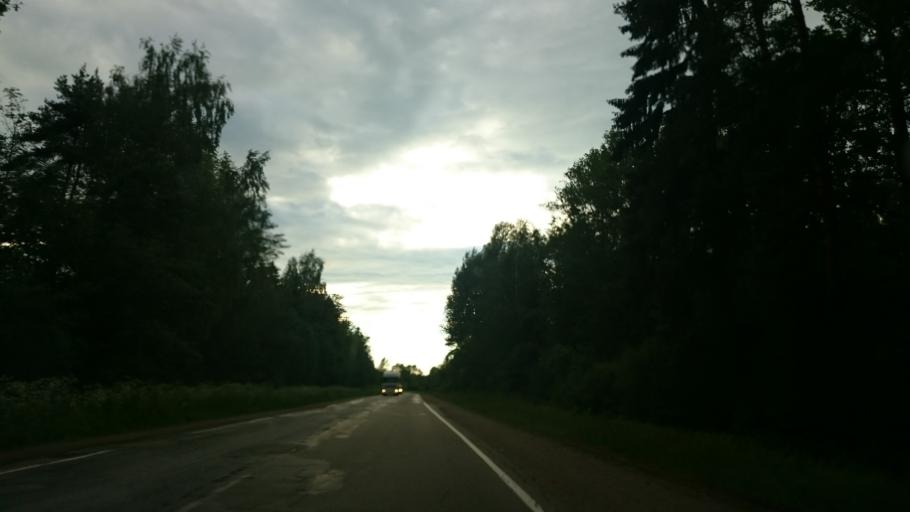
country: LV
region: Ludzas Rajons
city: Ludza
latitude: 56.5359
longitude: 27.6482
